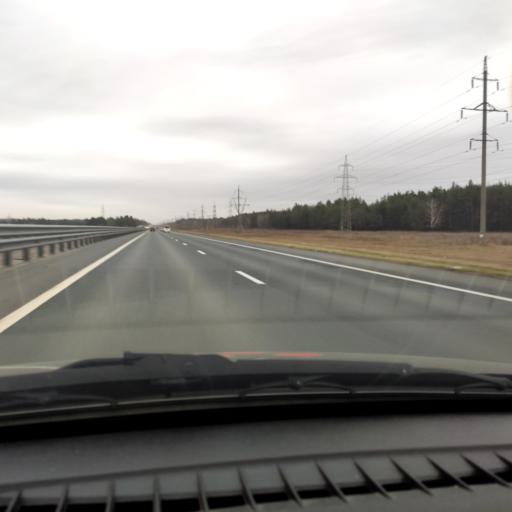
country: RU
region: Samara
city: Povolzhskiy
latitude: 53.5149
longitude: 49.6744
